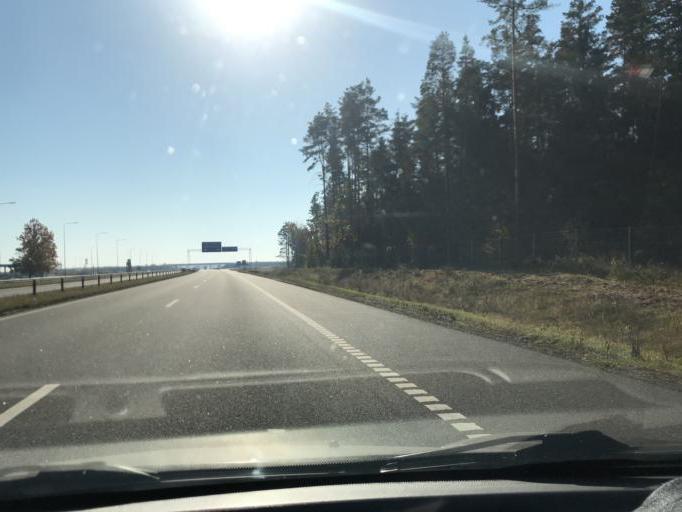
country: BY
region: Mogilev
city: Babruysk
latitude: 53.1917
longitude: 29.3531
